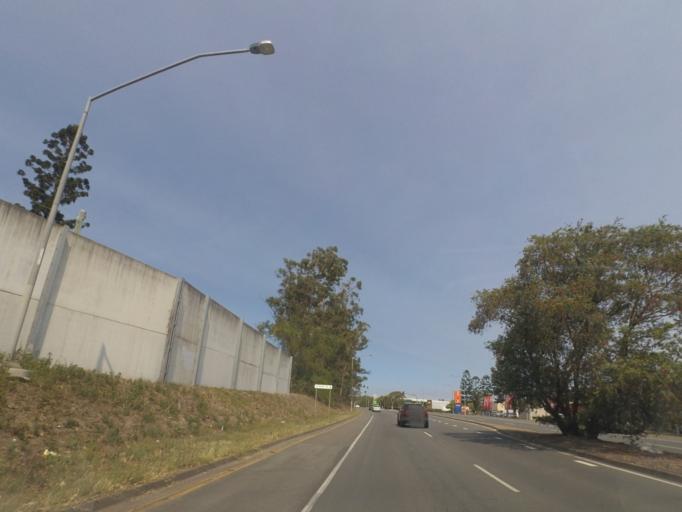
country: AU
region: Queensland
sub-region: Brisbane
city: Coopers Plains
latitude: -27.5578
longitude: 153.0291
